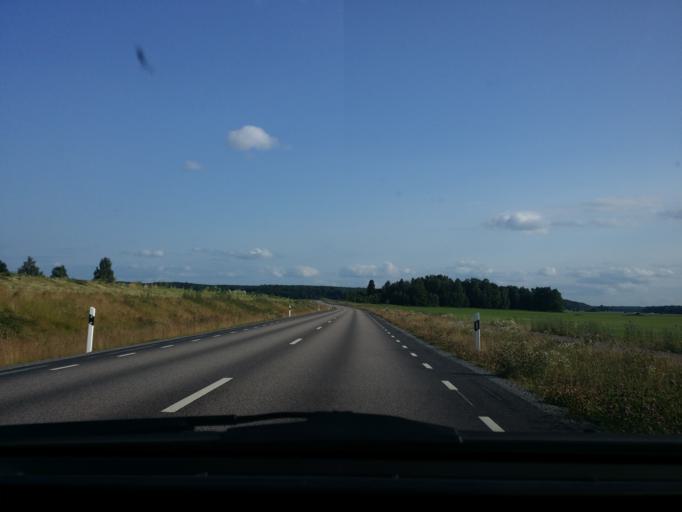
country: SE
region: Vaestmanland
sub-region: Vasteras
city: Tillberga
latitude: 59.5959
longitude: 16.6650
